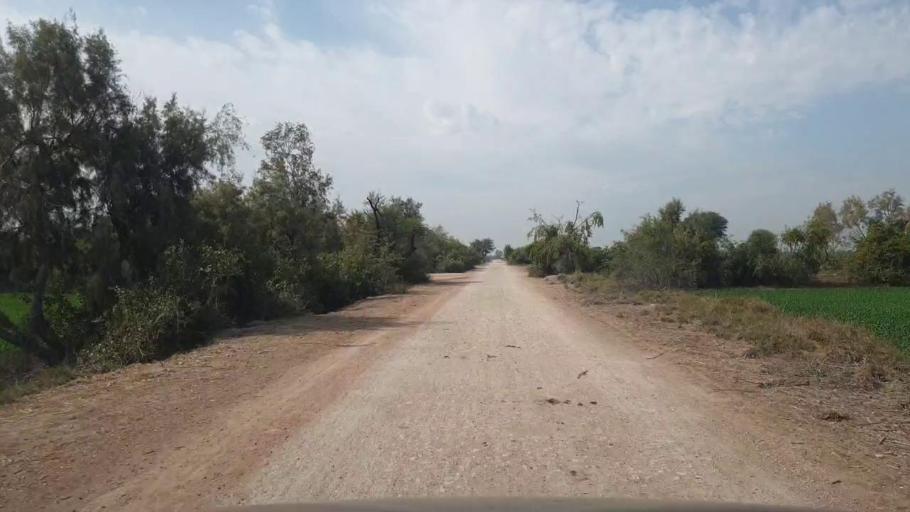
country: PK
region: Sindh
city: Sakrand
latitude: 25.9976
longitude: 68.3892
